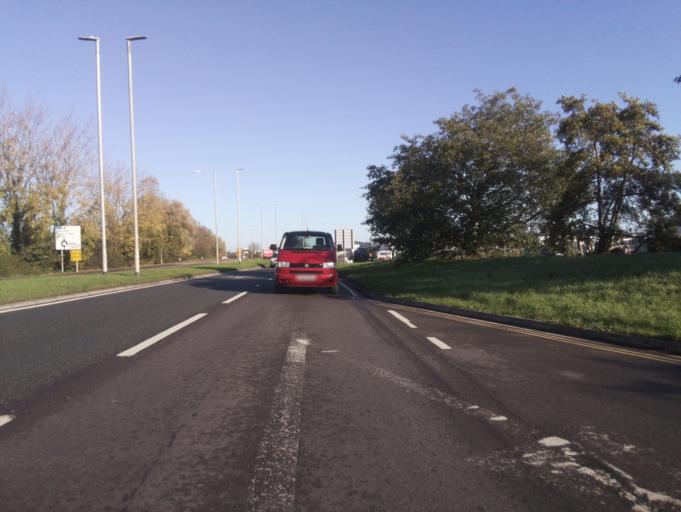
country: GB
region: England
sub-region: Somerset
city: Bridgwater
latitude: 51.1485
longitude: -2.9900
